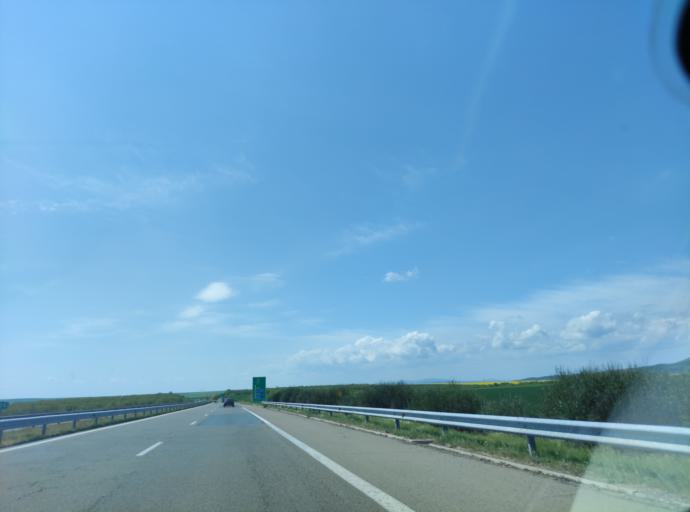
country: BG
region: Burgas
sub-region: Obshtina Karnobat
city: Karnobat
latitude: 42.5903
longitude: 26.9987
